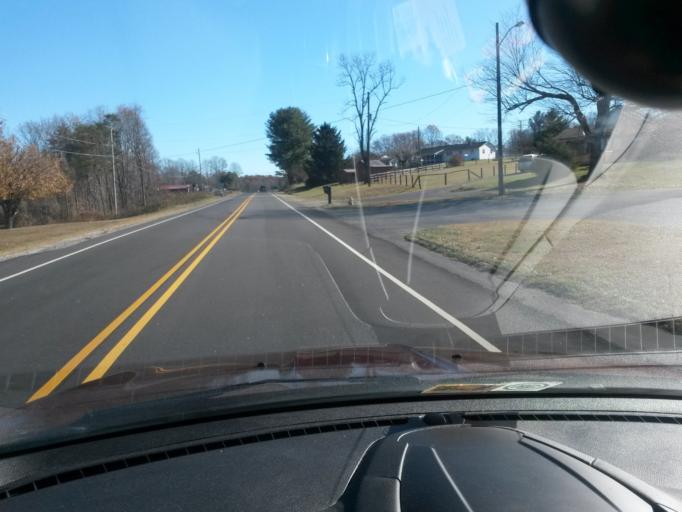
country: US
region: Virginia
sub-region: Henry County
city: Pannill Fork
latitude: 36.7508
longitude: -80.0750
